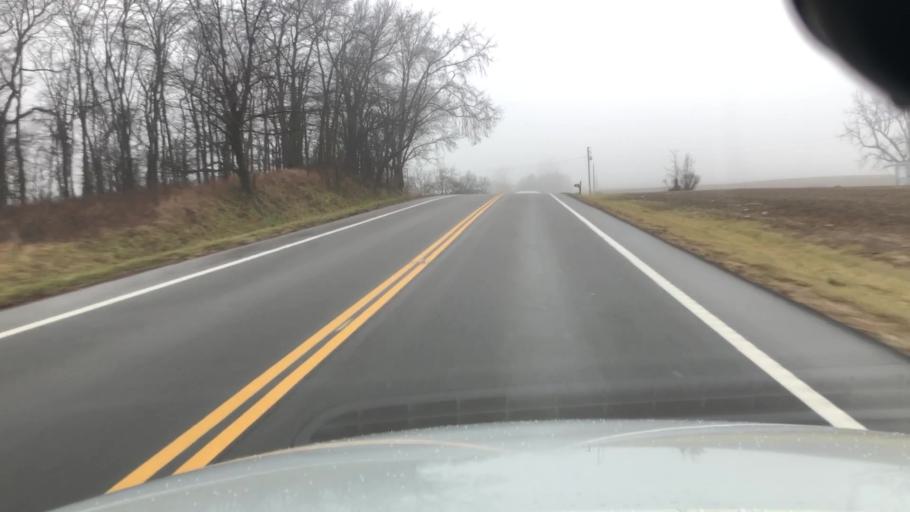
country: US
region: Ohio
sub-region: Logan County
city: Lakeview
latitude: 40.6079
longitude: -83.8893
